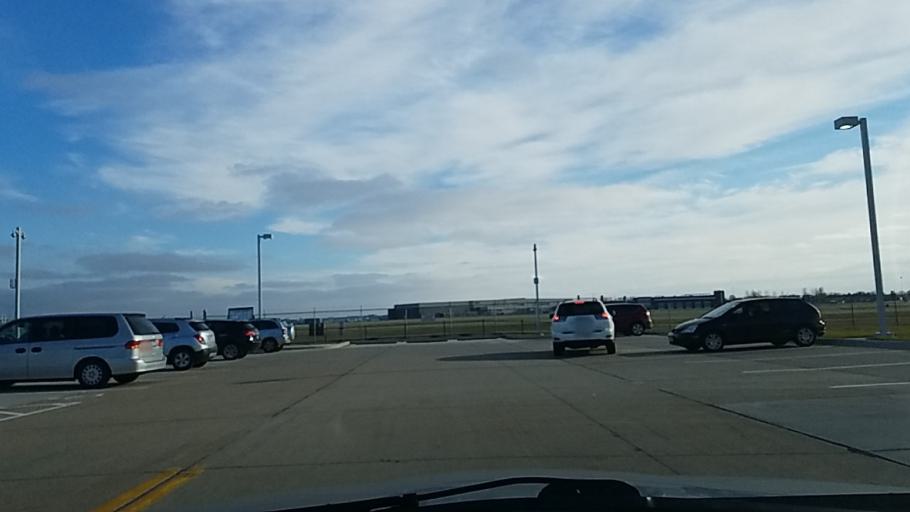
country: US
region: Minnesota
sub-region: Hennepin County
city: Richfield
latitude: 44.8822
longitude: -93.2291
